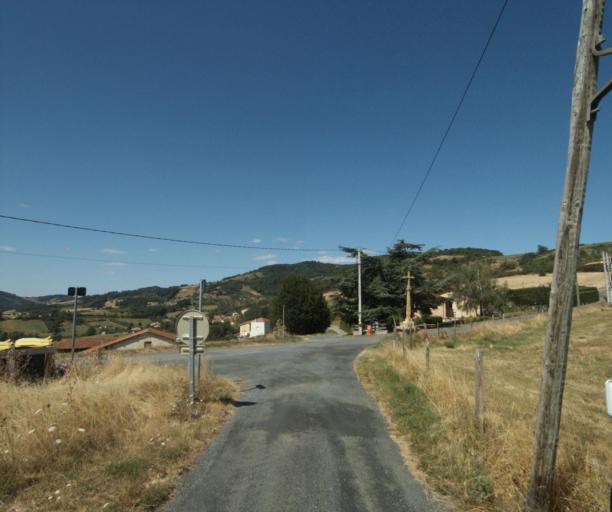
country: FR
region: Rhone-Alpes
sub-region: Departement du Rhone
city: Bessenay
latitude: 45.8065
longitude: 4.5296
